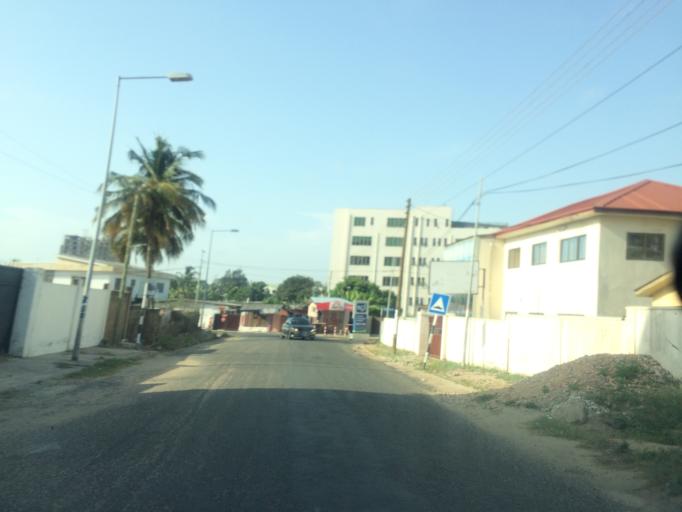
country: GH
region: Greater Accra
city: Accra
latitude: 5.5626
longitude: -0.1860
